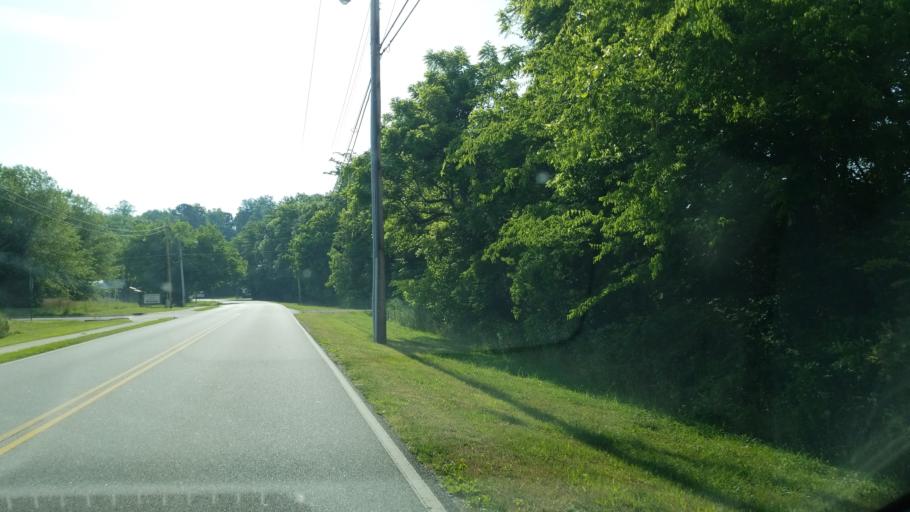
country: US
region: Tennessee
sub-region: Hamilton County
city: Collegedale
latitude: 35.0537
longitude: -85.0430
